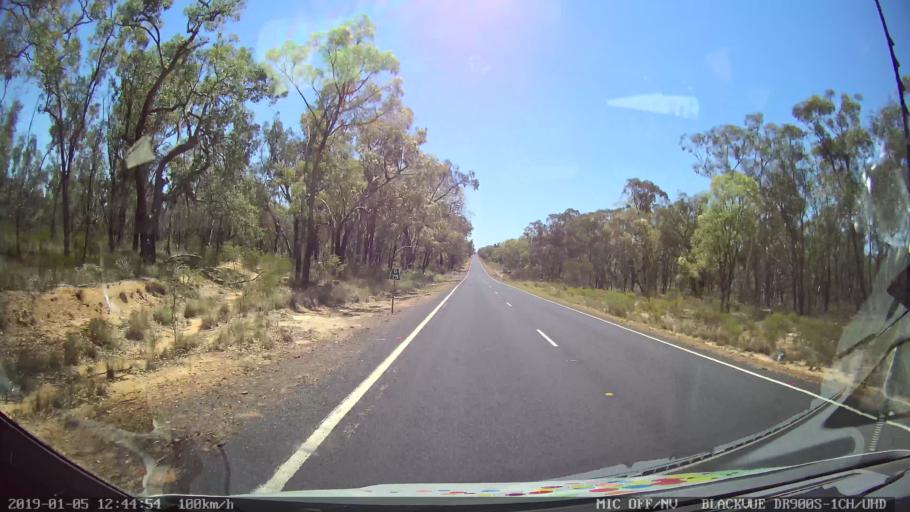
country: AU
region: New South Wales
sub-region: Warrumbungle Shire
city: Coonabarabran
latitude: -31.1332
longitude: 149.5431
